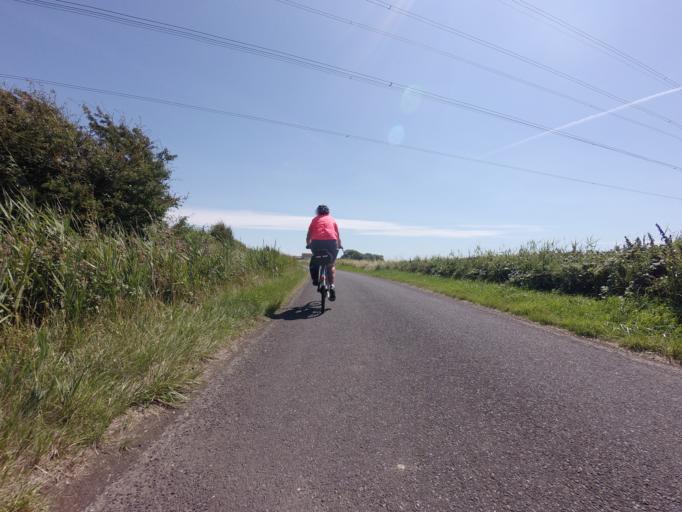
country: GB
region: England
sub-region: Kent
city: Lydd
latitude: 50.9768
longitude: 0.8995
